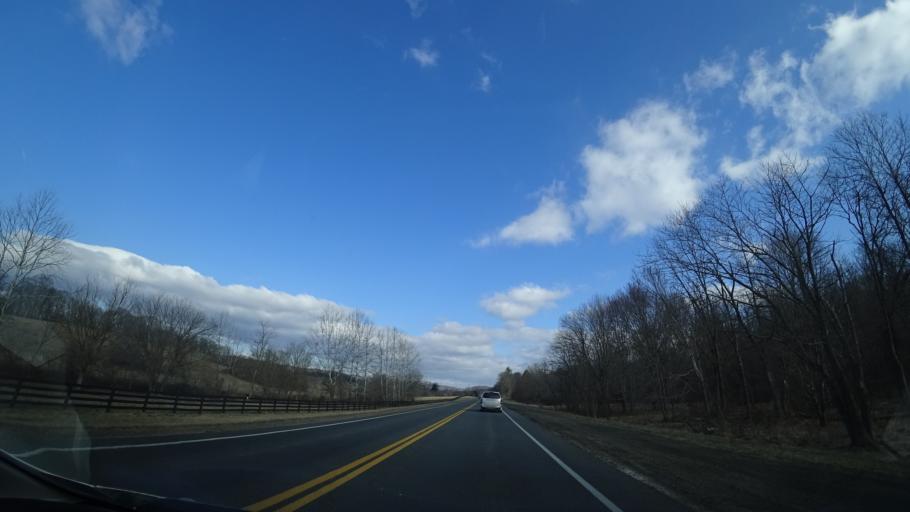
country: US
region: Virginia
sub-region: Fauquier County
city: Marshall
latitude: 38.9377
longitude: -77.9344
